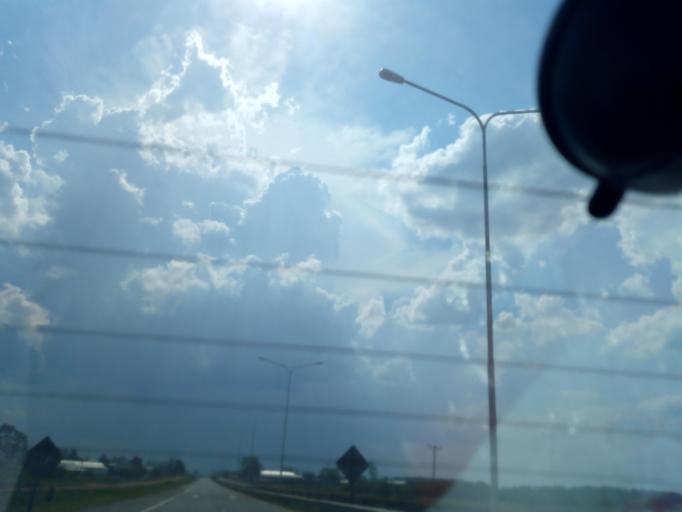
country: AR
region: Corrientes
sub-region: Departamento de Paso de los Libres
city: Paso de los Libres
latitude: -29.7220
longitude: -57.1557
